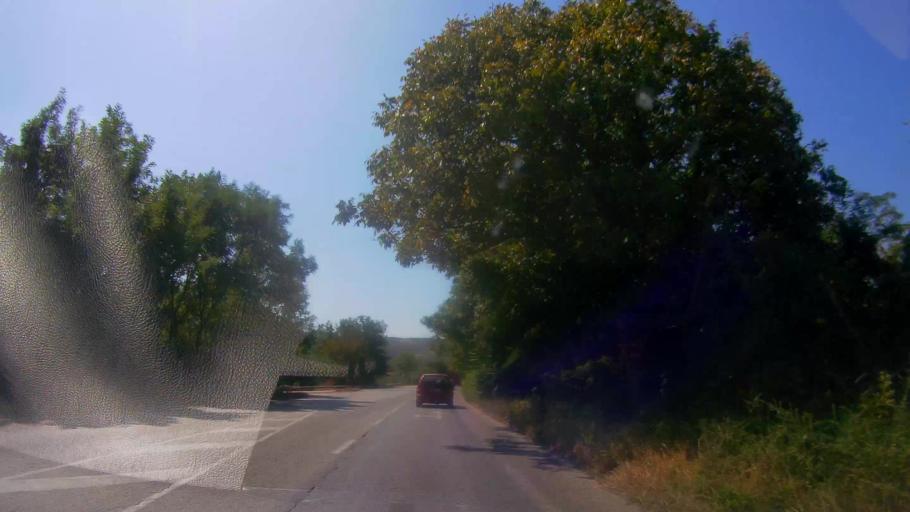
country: BG
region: Veliko Turnovo
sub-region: Obshtina Gorna Oryakhovitsa
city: Purvomaytsi
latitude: 43.1512
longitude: 25.6174
